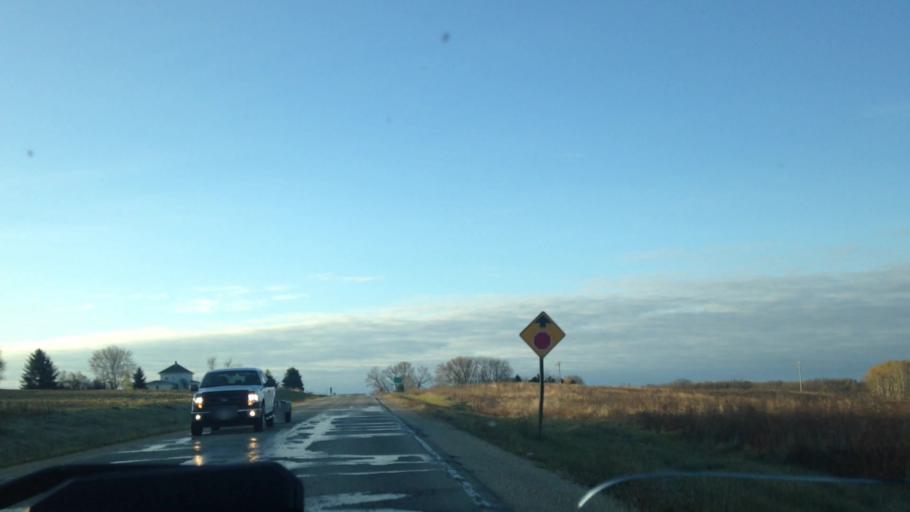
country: US
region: Wisconsin
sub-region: Dodge County
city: Mayville
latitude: 43.4456
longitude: -88.5001
